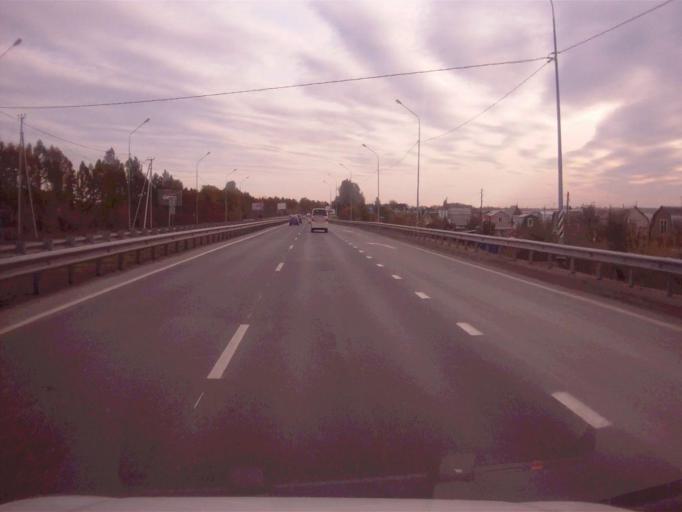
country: RU
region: Chelyabinsk
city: Novosineglazovskiy
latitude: 55.0306
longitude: 61.4465
